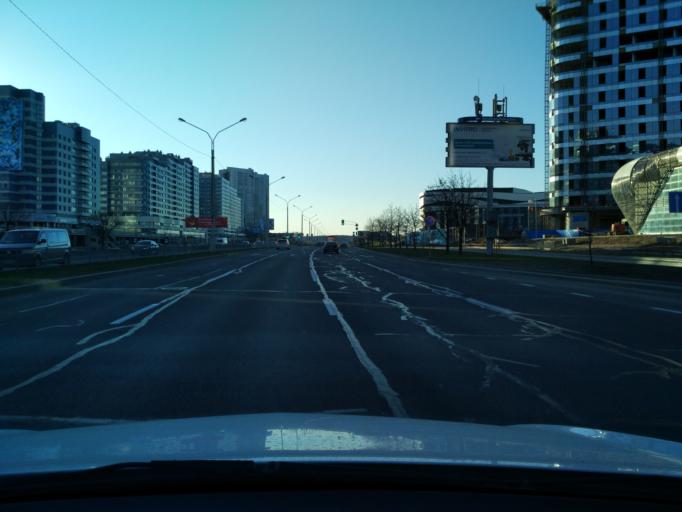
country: BY
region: Minsk
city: Zhdanovichy
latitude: 53.9398
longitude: 27.4714
